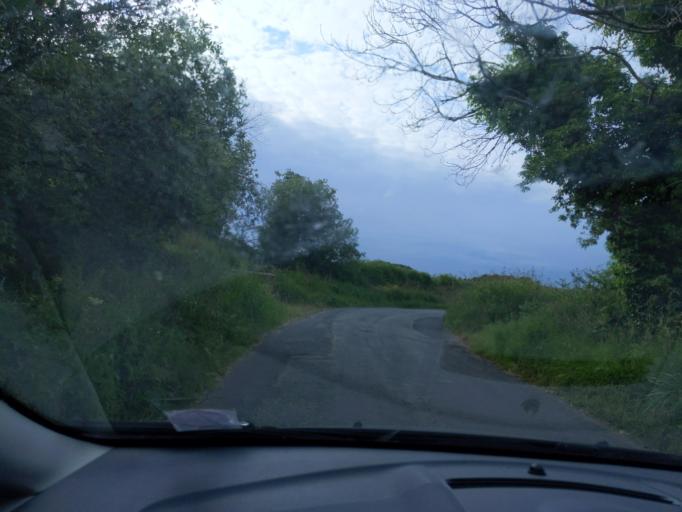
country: IM
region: Ramsey
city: Ramsey
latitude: 54.3500
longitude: -4.4501
